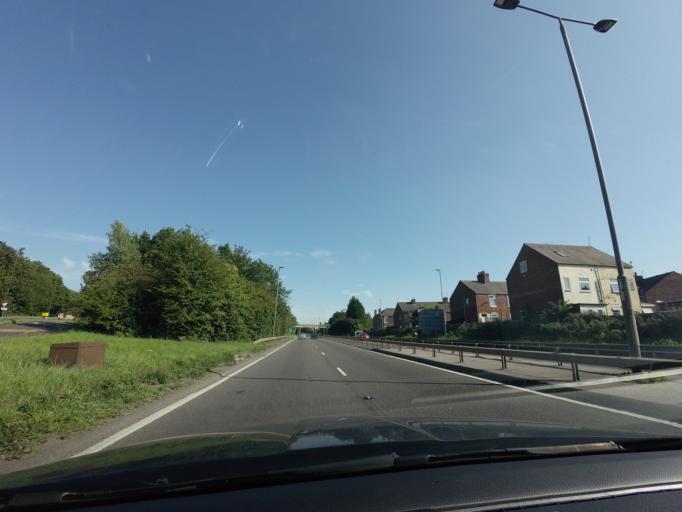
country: GB
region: England
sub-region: Derbyshire
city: Chesterfield
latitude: 53.2294
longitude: -1.4183
